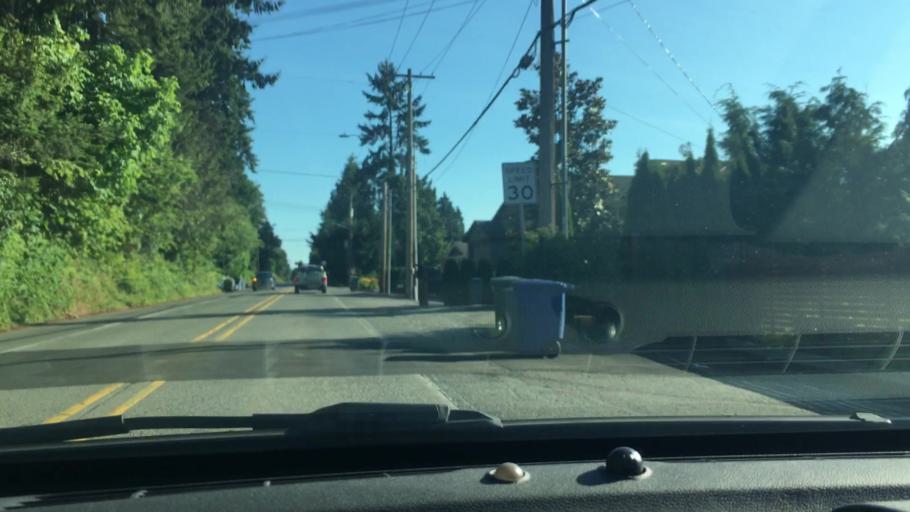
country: US
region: Washington
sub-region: King County
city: West Lake Sammamish
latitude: 47.5799
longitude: -122.1130
